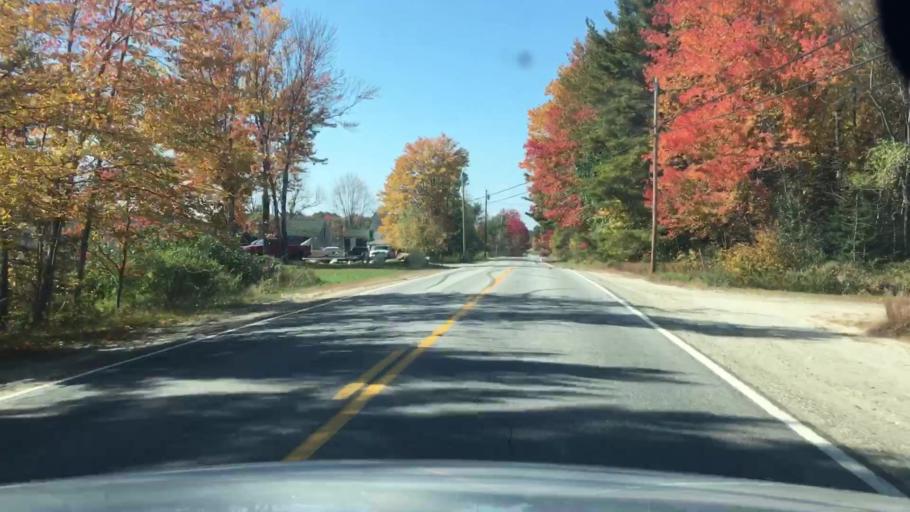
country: US
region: Maine
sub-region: Androscoggin County
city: Lisbon Falls
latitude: 44.0402
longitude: -69.9979
